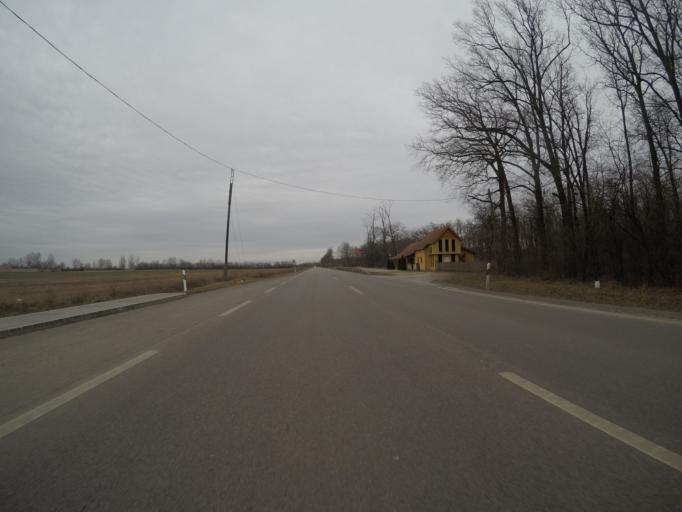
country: HU
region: Jasz-Nagykun-Szolnok
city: Jaszjakohalma
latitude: 47.5126
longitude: 20.0586
